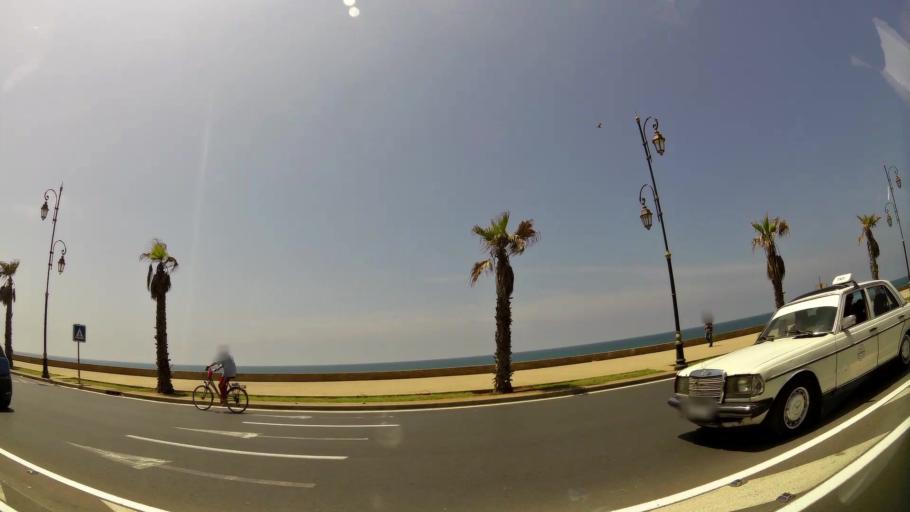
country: MA
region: Rabat-Sale-Zemmour-Zaer
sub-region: Rabat
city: Rabat
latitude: 34.0091
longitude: -6.8668
